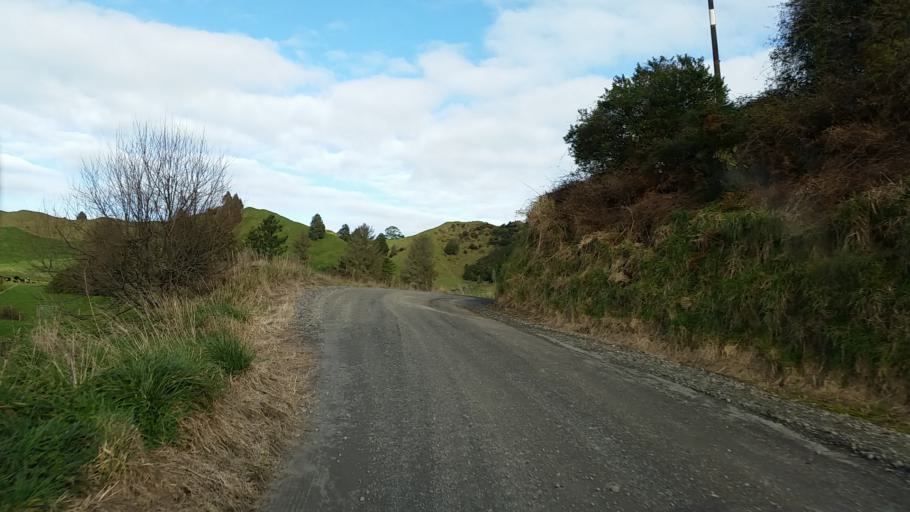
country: NZ
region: Taranaki
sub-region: South Taranaki District
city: Eltham
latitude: -39.2557
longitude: 174.5264
